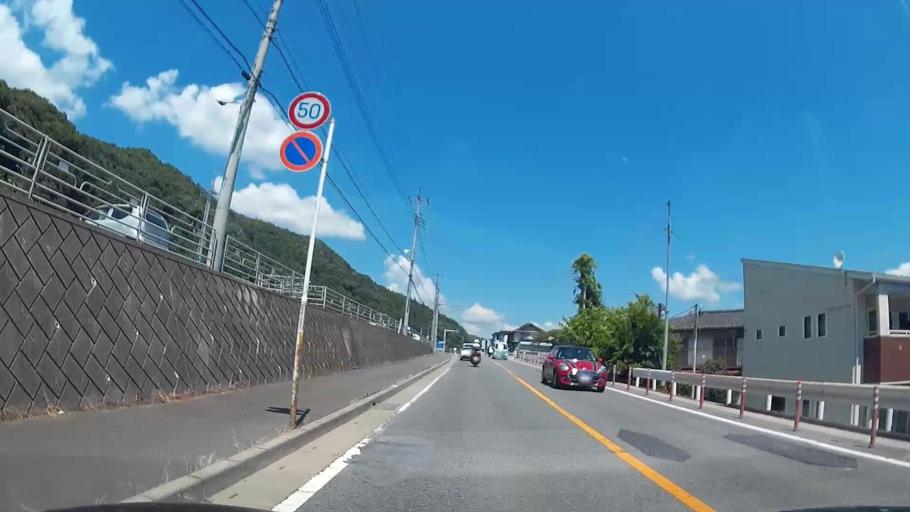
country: JP
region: Gunma
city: Numata
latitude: 36.6020
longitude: 139.0484
